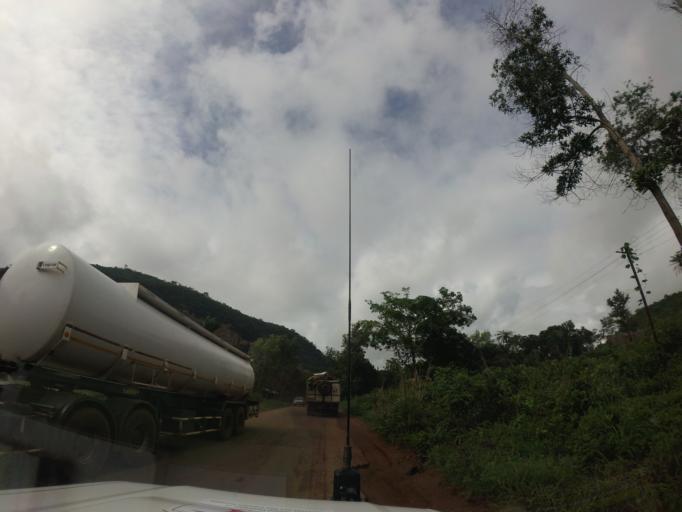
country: GN
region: Kindia
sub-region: Coyah
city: Coyah
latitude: 9.7715
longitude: -13.3453
